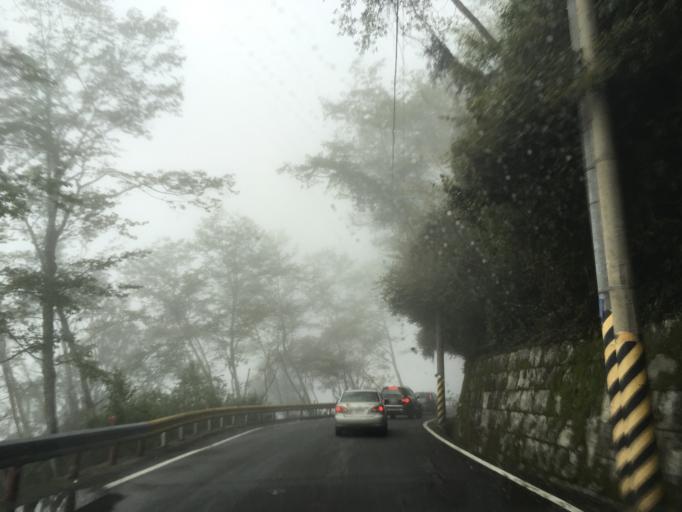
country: TW
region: Taiwan
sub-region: Hualien
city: Hualian
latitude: 24.1882
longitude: 121.4096
